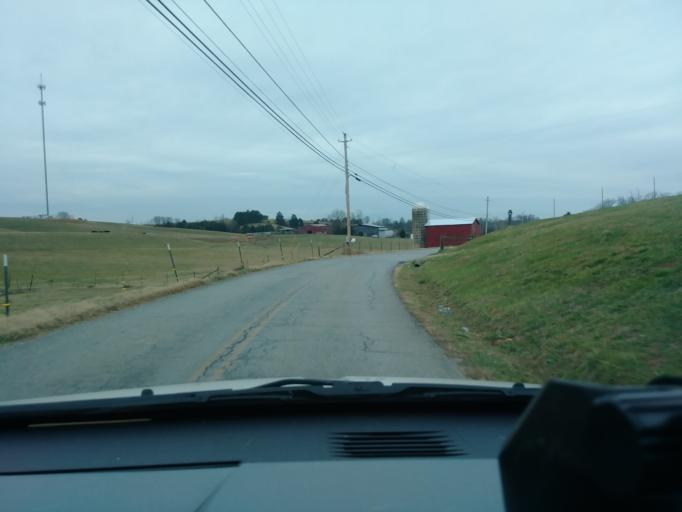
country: US
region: Tennessee
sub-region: Greene County
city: Greeneville
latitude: 36.1094
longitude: -82.8826
